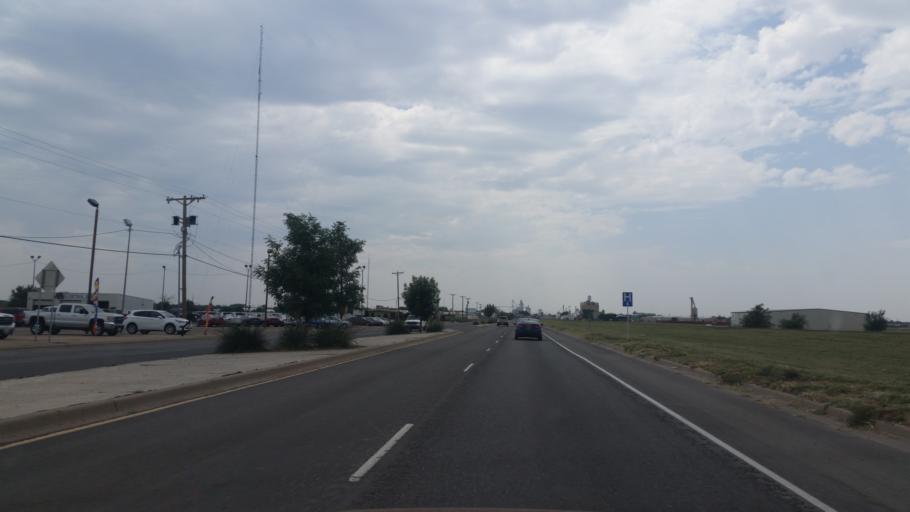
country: US
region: New Mexico
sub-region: Roosevelt County
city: Portales
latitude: 34.2000
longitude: -103.3215
